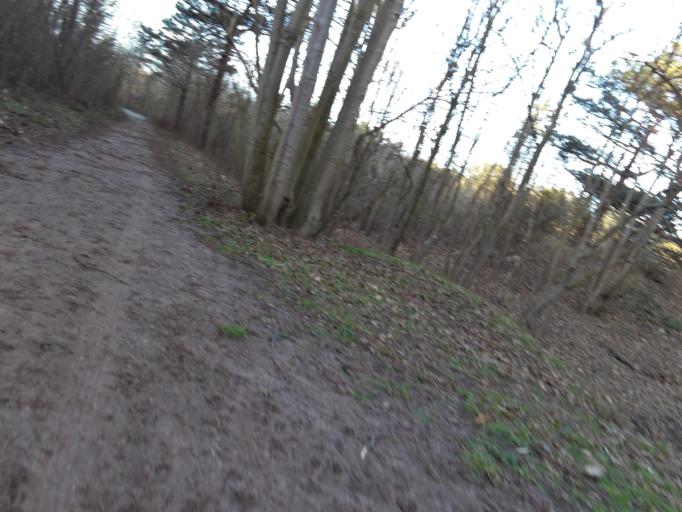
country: NL
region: South Holland
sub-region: Gemeente Noordwijkerhout
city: Noordwijkerhout
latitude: 52.2700
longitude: 4.4632
